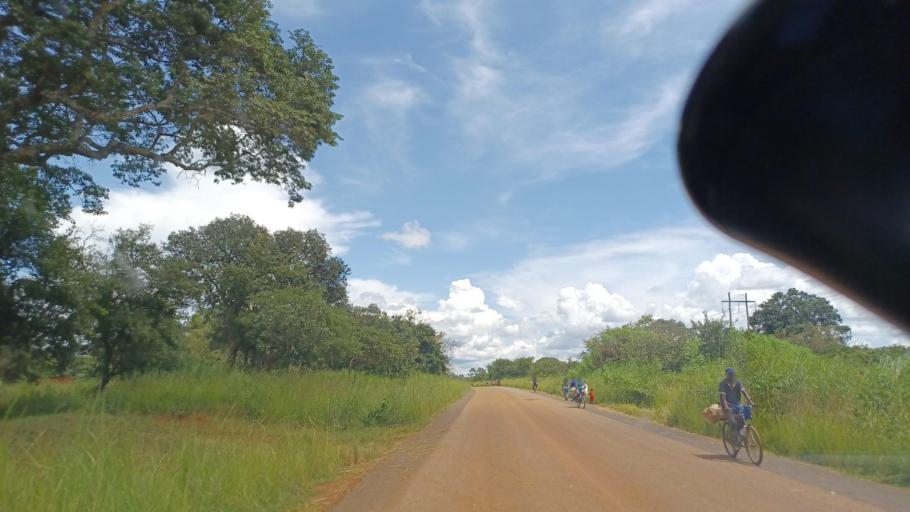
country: ZM
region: North-Western
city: Solwezi
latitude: -12.5584
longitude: 26.1430
